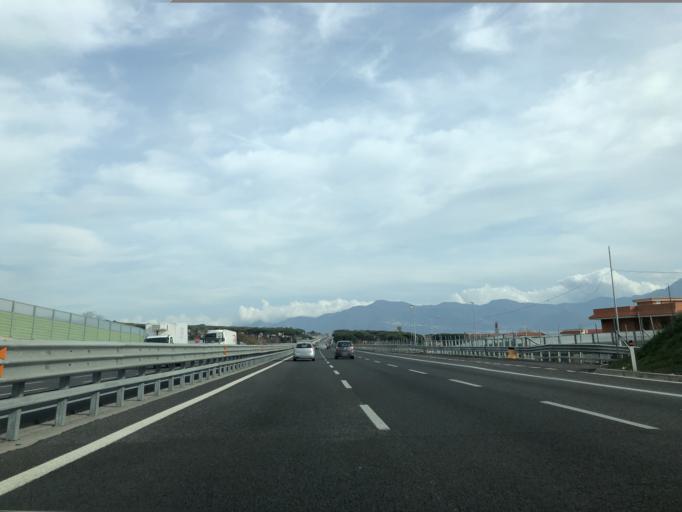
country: IT
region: Campania
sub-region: Provincia di Napoli
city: Torre del Greco
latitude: 40.7776
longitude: 14.3980
